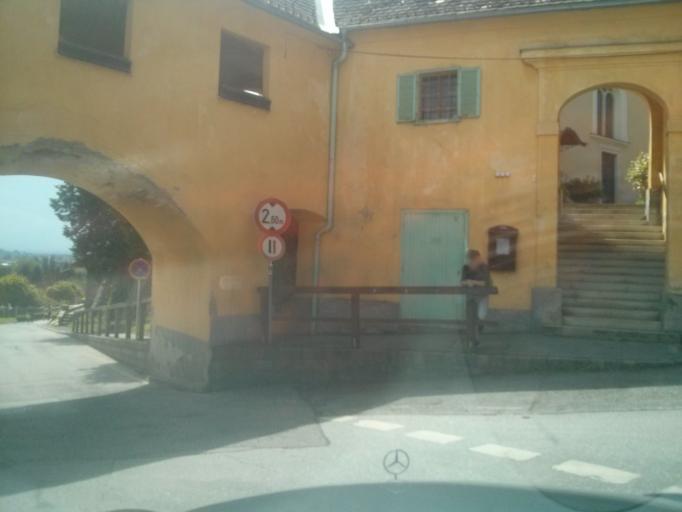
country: AT
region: Styria
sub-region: Politischer Bezirk Graz-Umgebung
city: Stattegg
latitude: 47.1163
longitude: 15.4117
